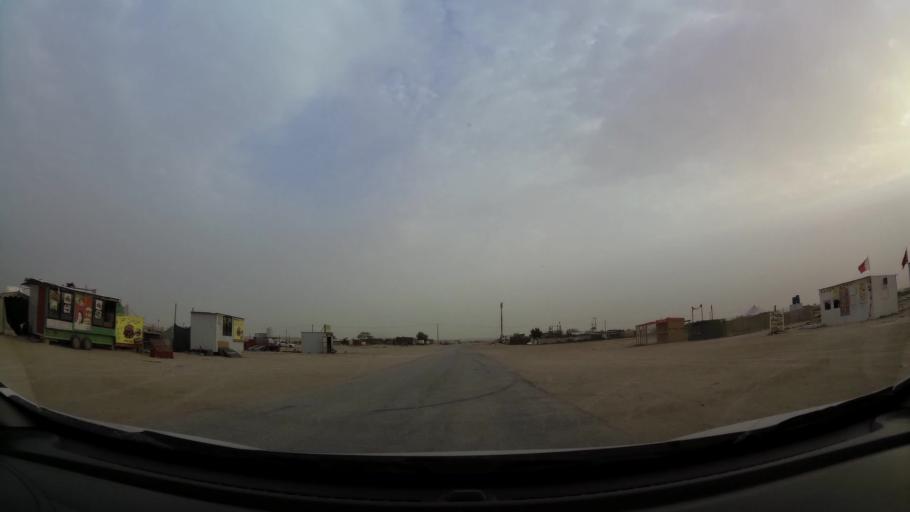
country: BH
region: Central Governorate
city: Dar Kulayb
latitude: 26.0035
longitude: 50.5854
